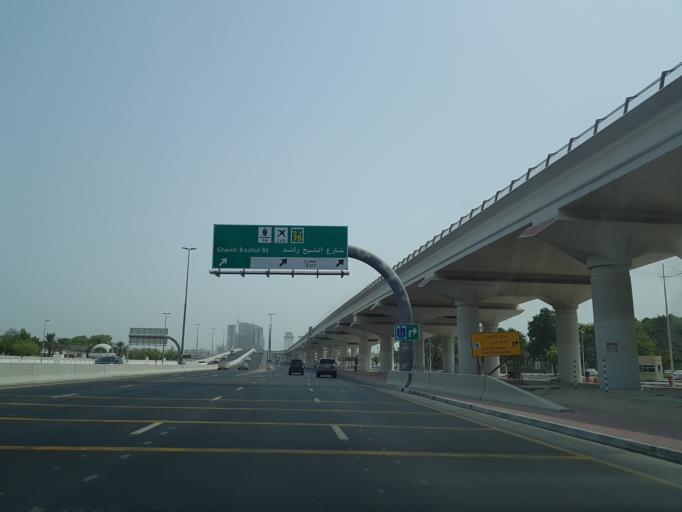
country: AE
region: Ash Shariqah
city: Sharjah
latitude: 25.2354
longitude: 55.2931
